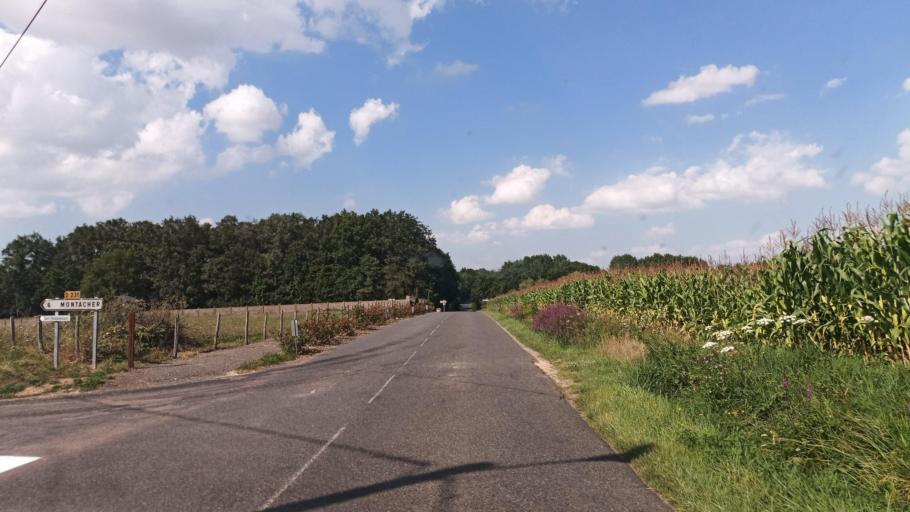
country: FR
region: Bourgogne
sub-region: Departement de l'Yonne
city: Saint-Valerien
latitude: 48.1491
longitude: 3.0900
